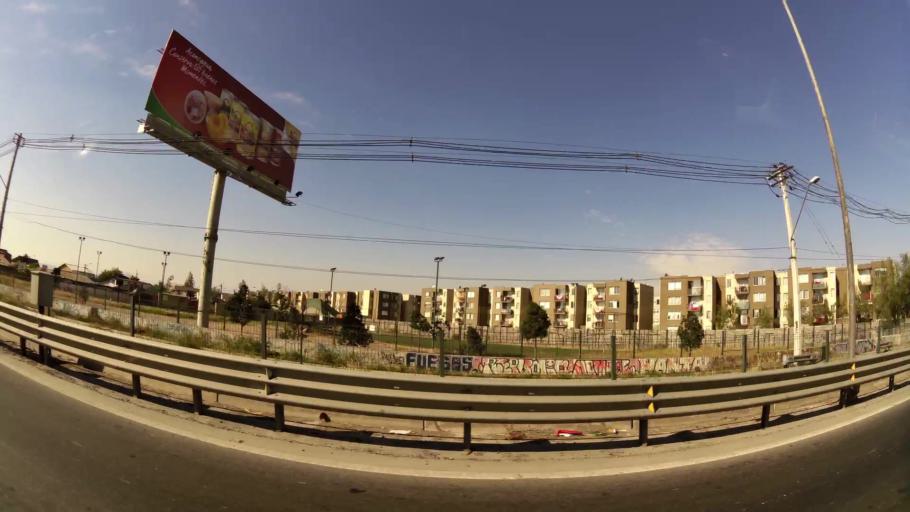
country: CL
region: Santiago Metropolitan
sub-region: Provincia de Santiago
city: Lo Prado
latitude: -33.5000
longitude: -70.7427
